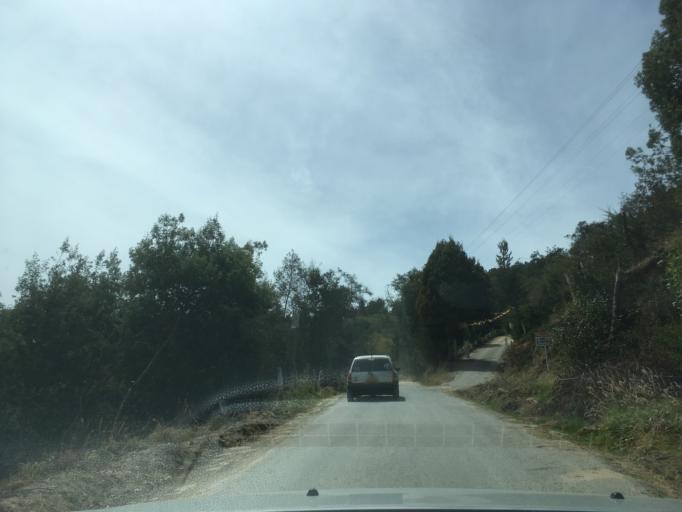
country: CO
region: Boyaca
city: Aquitania
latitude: 5.5854
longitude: -72.9242
